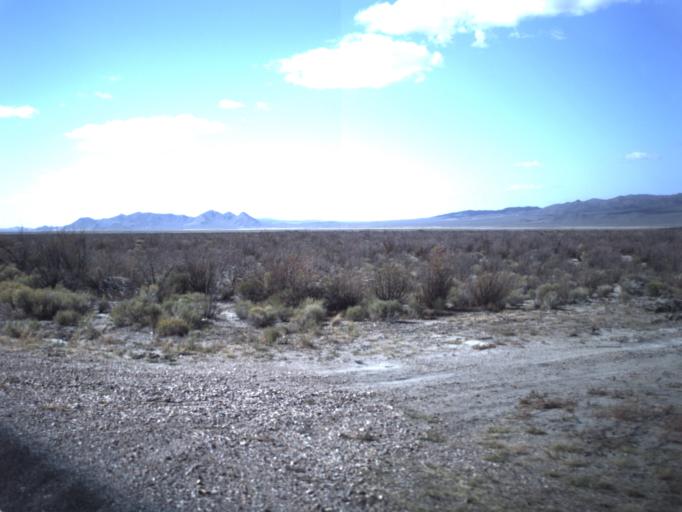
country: US
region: Utah
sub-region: Beaver County
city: Milford
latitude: 38.5724
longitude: -112.9899
